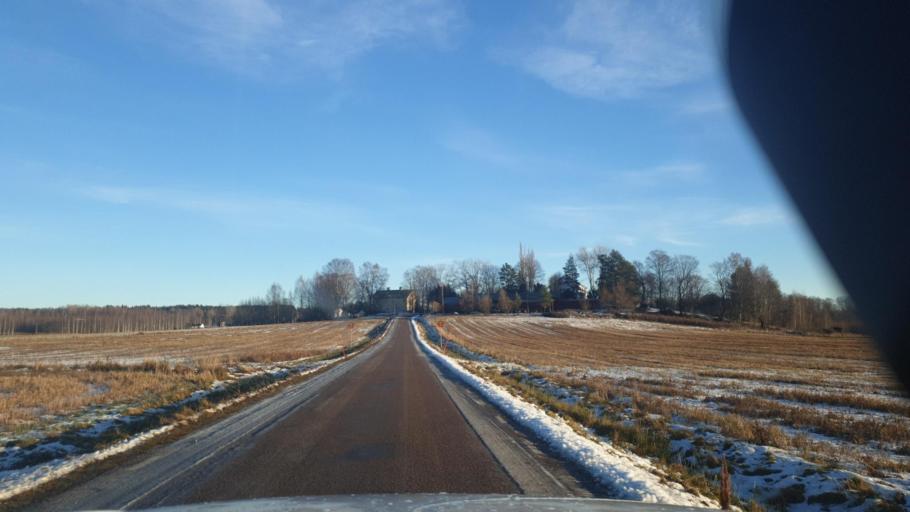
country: SE
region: Vaermland
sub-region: Arvika Kommun
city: Arvika
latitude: 59.5488
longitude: 12.5500
